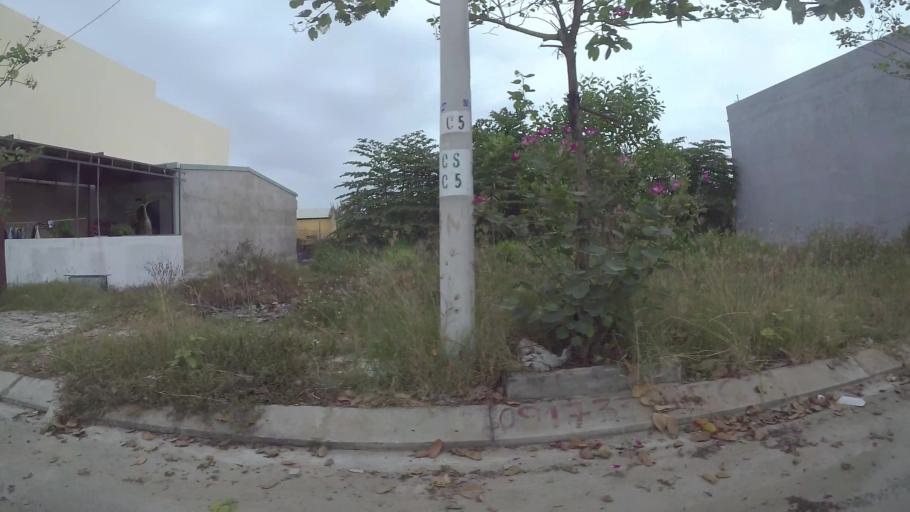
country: VN
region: Da Nang
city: Cam Le
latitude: 16.0380
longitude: 108.1747
